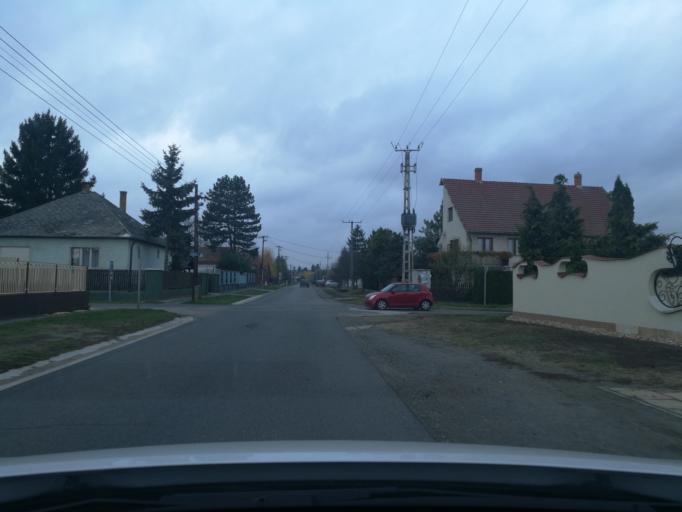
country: HU
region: Szabolcs-Szatmar-Bereg
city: Nyirpazony
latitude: 47.9807
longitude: 21.7915
